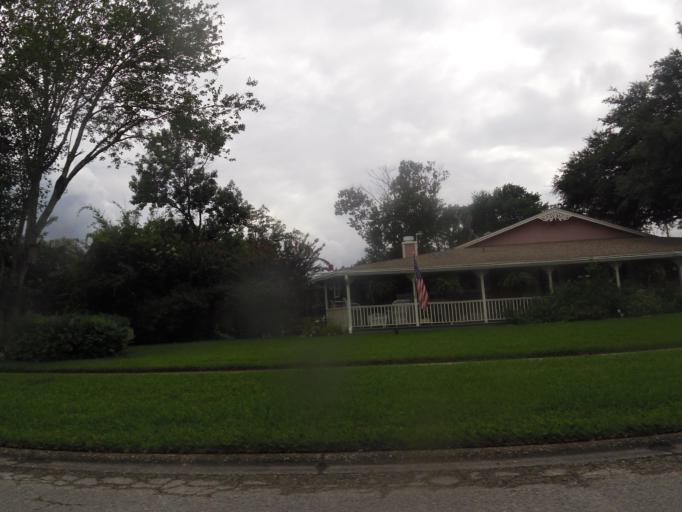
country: US
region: Florida
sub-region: Duval County
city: Jacksonville Beach
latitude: 30.2723
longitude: -81.4346
